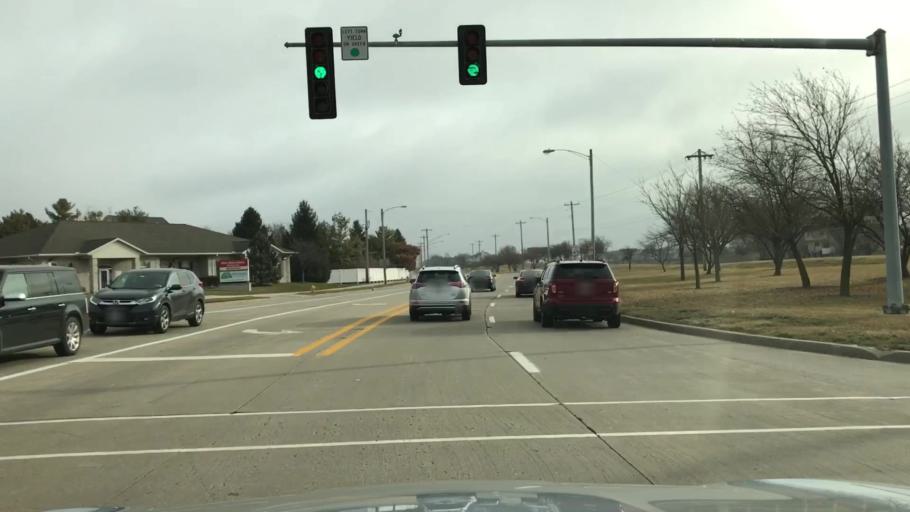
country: US
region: Illinois
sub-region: McLean County
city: Normal
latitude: 40.5027
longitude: -88.9240
